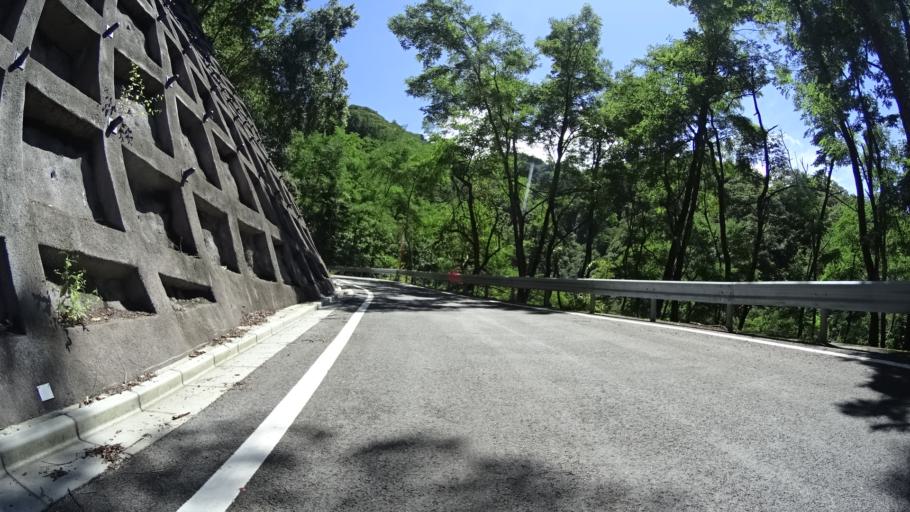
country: JP
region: Yamanashi
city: Enzan
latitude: 35.7398
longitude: 138.8288
